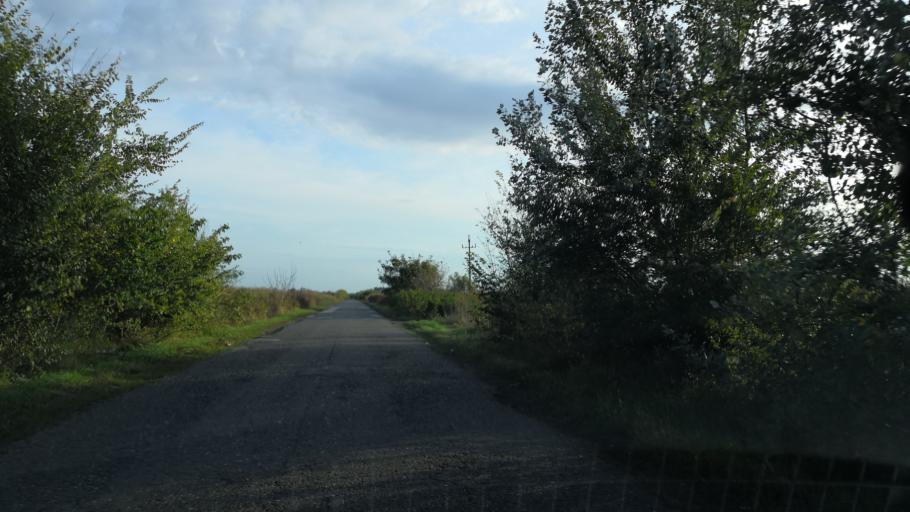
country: RS
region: Autonomna Pokrajina Vojvodina
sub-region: Sremski Okrug
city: Stara Pazova
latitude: 45.0066
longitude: 20.1664
